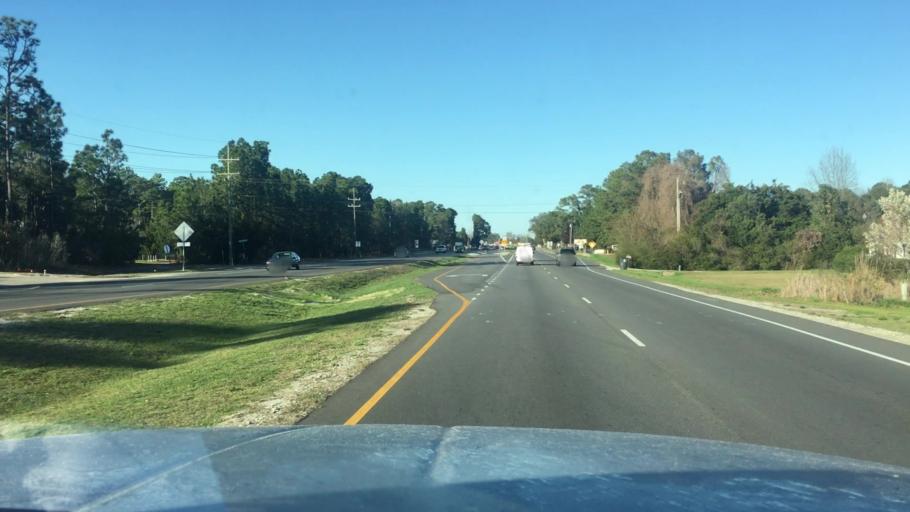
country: US
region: North Carolina
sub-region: New Hanover County
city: Myrtle Grove
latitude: 34.1281
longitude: -77.8982
